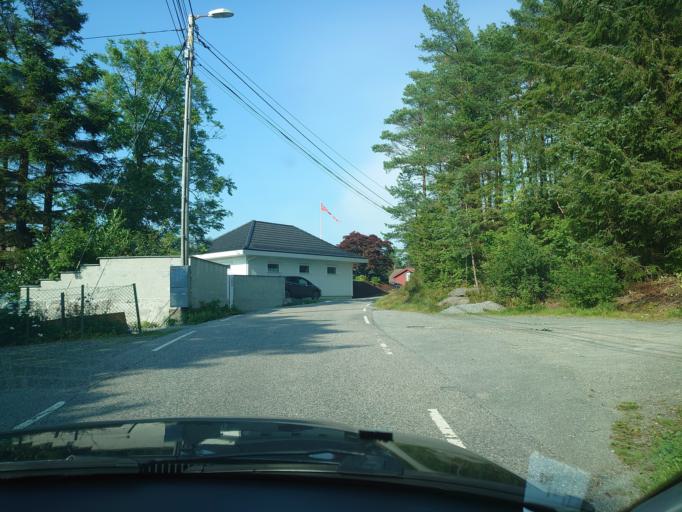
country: NO
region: Hordaland
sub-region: Bergen
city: Ytrebygda
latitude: 60.2678
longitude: 5.2602
